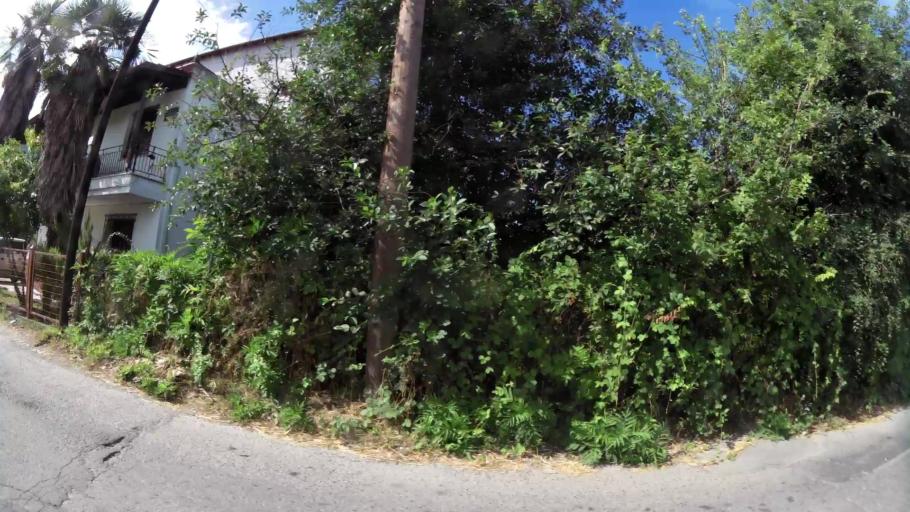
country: GR
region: Central Macedonia
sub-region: Nomos Pierias
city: Katerini
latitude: 40.2785
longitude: 22.5093
